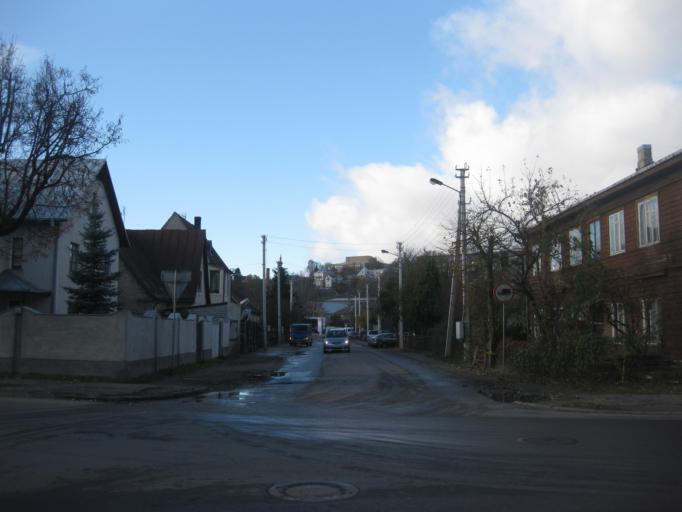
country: LT
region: Kauno apskritis
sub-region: Kaunas
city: Silainiai
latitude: 54.9133
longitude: 23.8904
